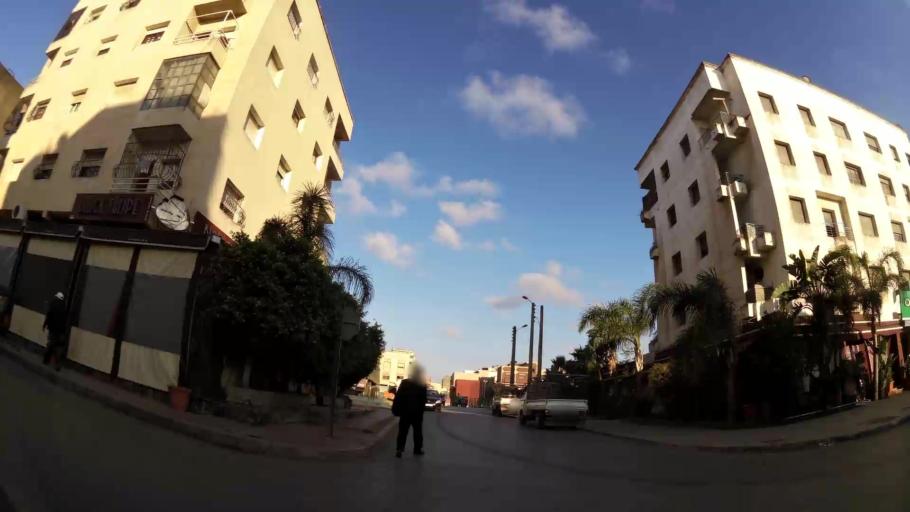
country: MA
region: Rabat-Sale-Zemmour-Zaer
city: Sale
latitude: 34.0601
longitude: -6.7843
